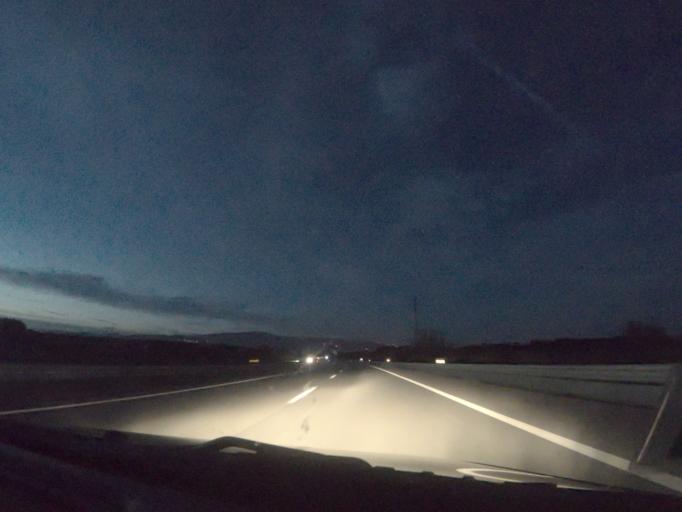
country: PT
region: Guarda
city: Alcains
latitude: 39.9591
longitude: -7.4558
